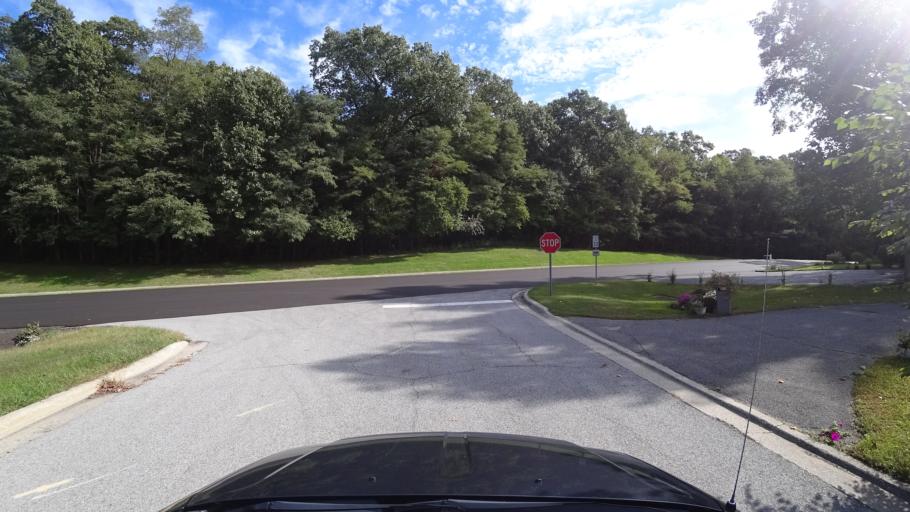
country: US
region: Indiana
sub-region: LaPorte County
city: Long Beach
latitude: 41.7216
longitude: -86.8744
